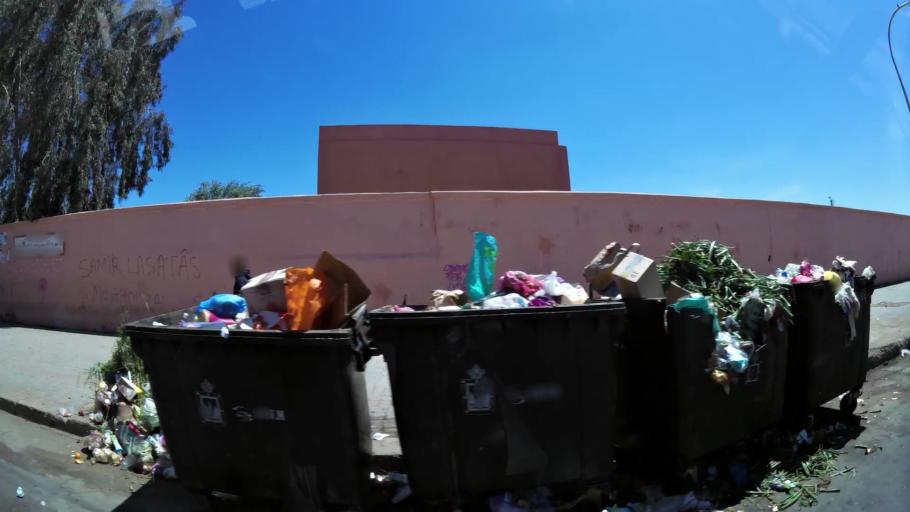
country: MA
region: Marrakech-Tensift-Al Haouz
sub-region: Marrakech
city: Marrakesh
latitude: 31.6308
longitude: -8.0506
